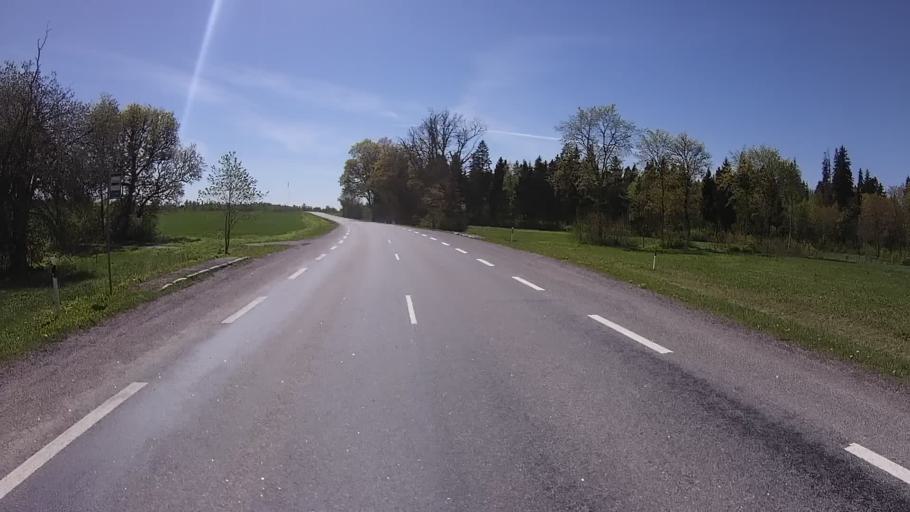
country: EE
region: Harju
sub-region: Raasiku vald
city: Raasiku
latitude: 59.0794
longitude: 25.1668
